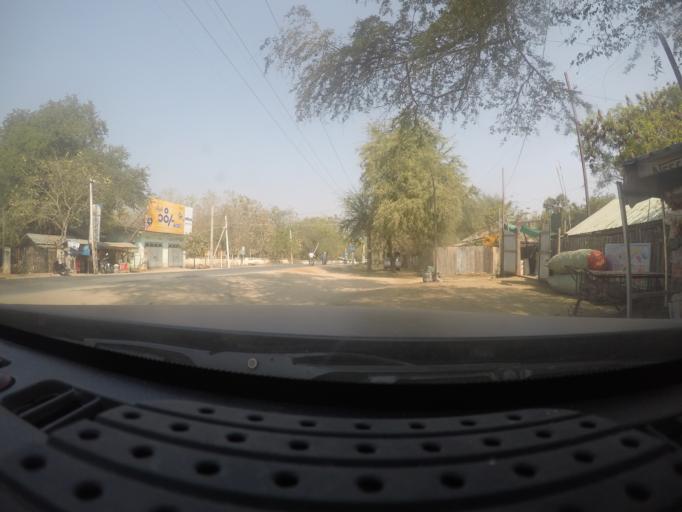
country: MM
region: Sagain
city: Sagaing
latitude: 21.9069
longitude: 95.9674
